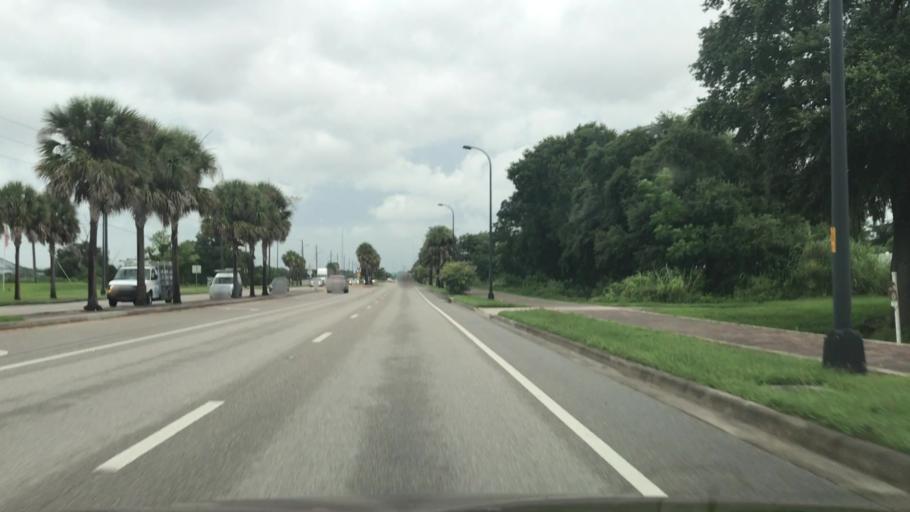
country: US
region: Florida
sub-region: Sarasota County
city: Fruitville
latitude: 27.3385
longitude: -82.4298
